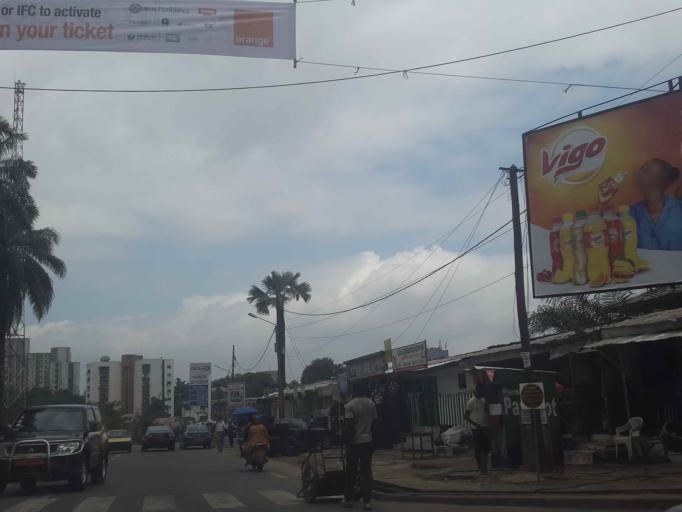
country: CM
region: Littoral
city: Douala
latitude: 4.0361
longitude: 9.6918
